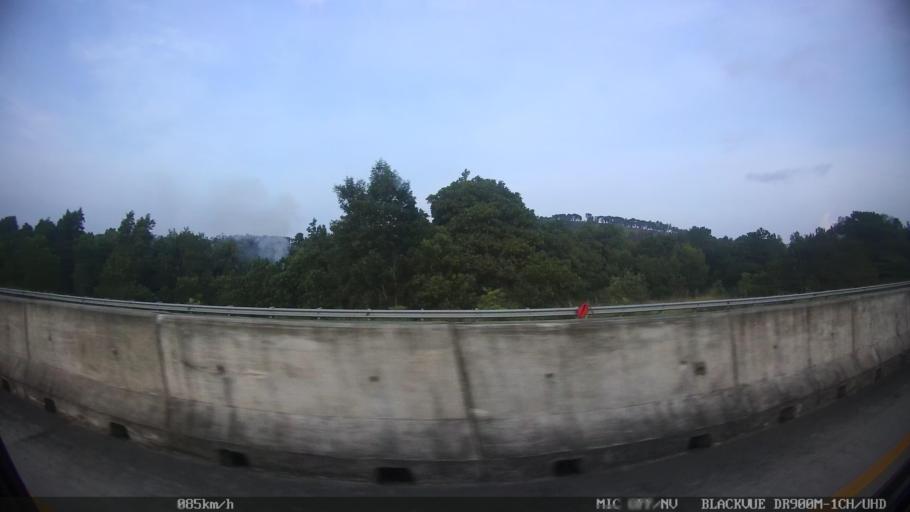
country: ID
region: Lampung
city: Penengahan
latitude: -5.8491
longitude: 105.7274
